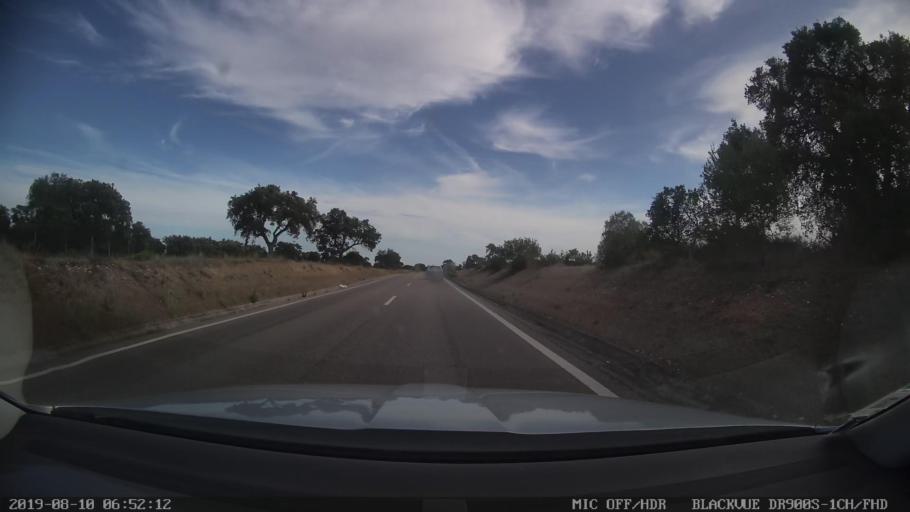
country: PT
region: Santarem
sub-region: Benavente
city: Poceirao
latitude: 38.8837
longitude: -8.7446
